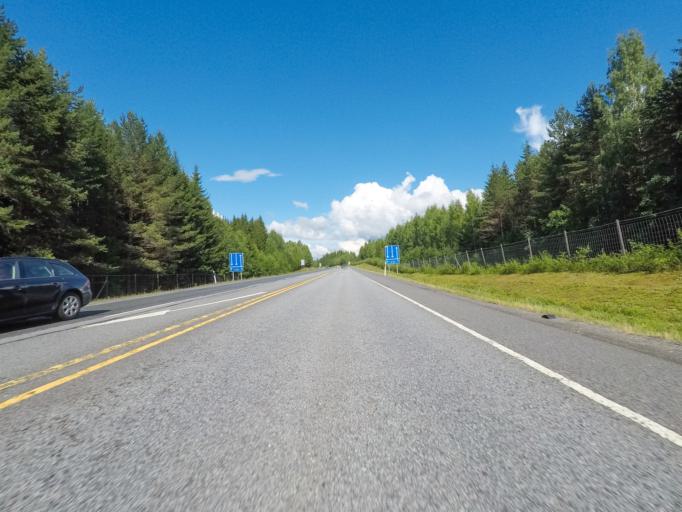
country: FI
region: Southern Savonia
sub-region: Mikkeli
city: Maentyharju
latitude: 61.5421
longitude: 26.9093
